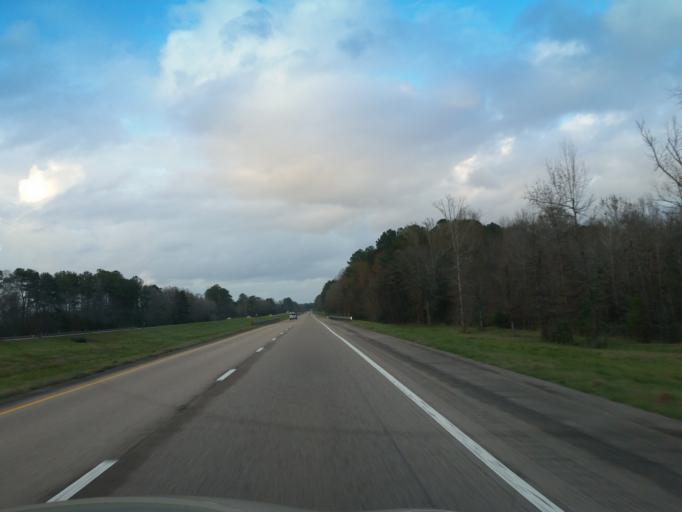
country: US
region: Mississippi
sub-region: Clarke County
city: Stonewall
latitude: 32.0243
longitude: -88.9225
